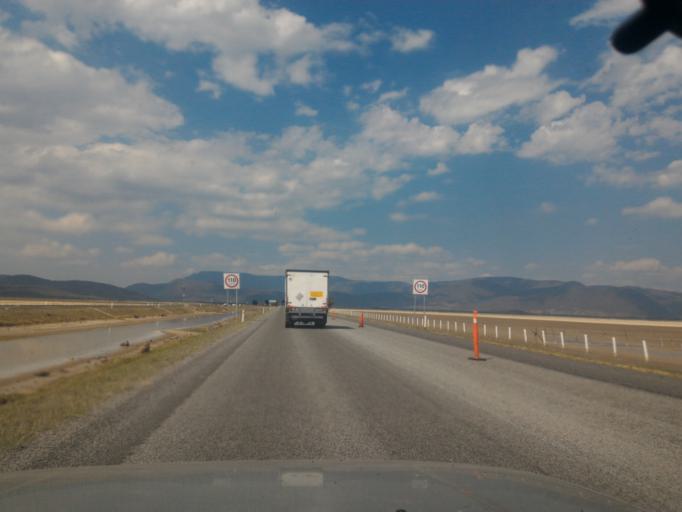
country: MX
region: Jalisco
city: Atoyac
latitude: 20.1053
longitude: -103.5126
